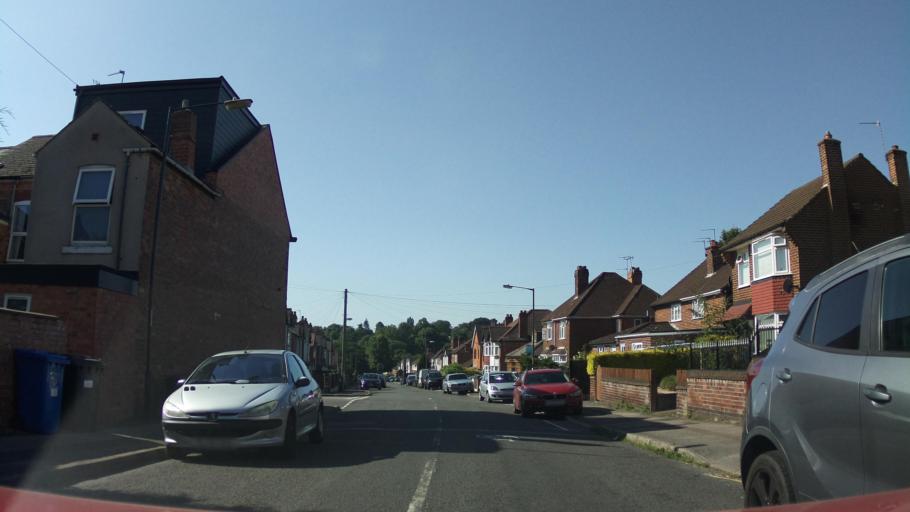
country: GB
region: England
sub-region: Derby
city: Derby
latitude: 52.9157
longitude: -1.4973
